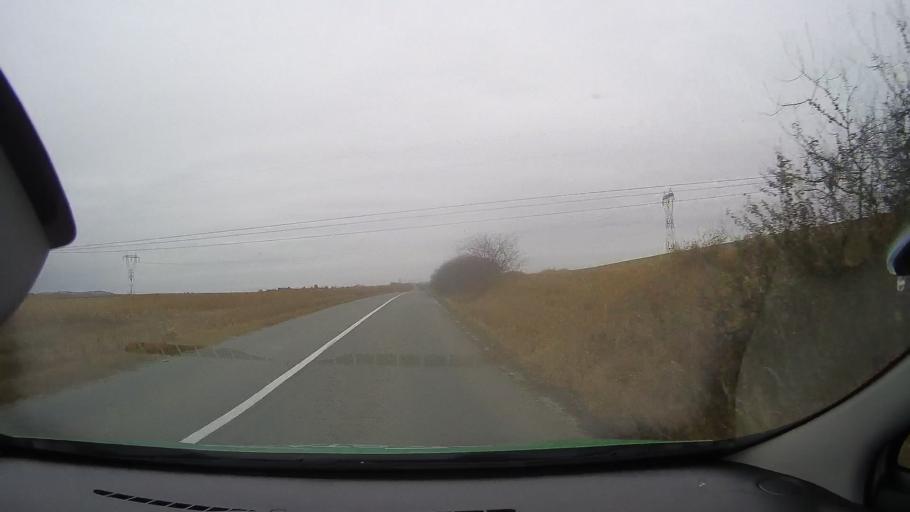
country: RO
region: Constanta
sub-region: Comuna Silistea
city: Silistea
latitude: 44.4346
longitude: 28.2206
